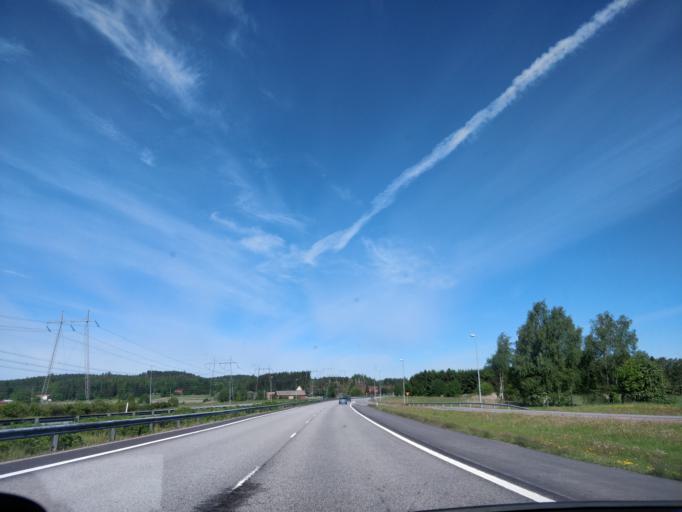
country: FI
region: Varsinais-Suomi
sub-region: Turku
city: Paimio
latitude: 60.4262
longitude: 22.6676
